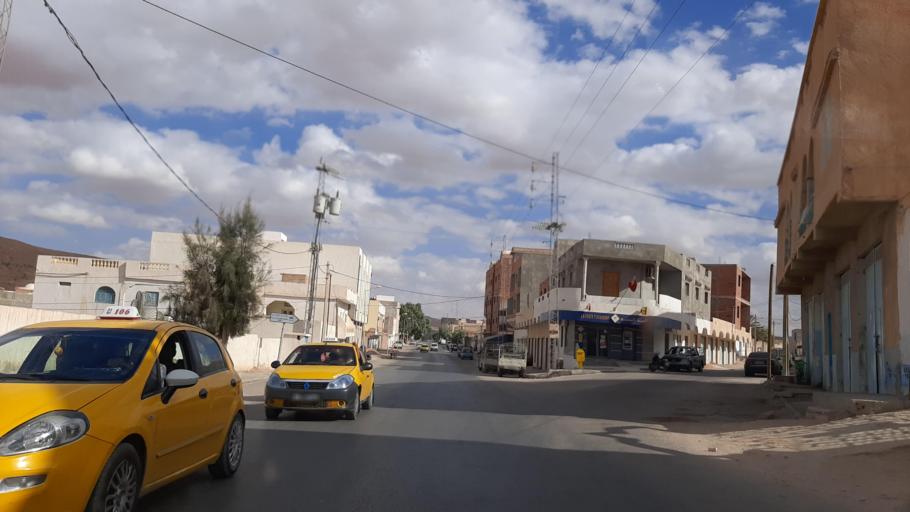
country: TN
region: Tataouine
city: Tataouine
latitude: 32.9237
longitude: 10.4573
